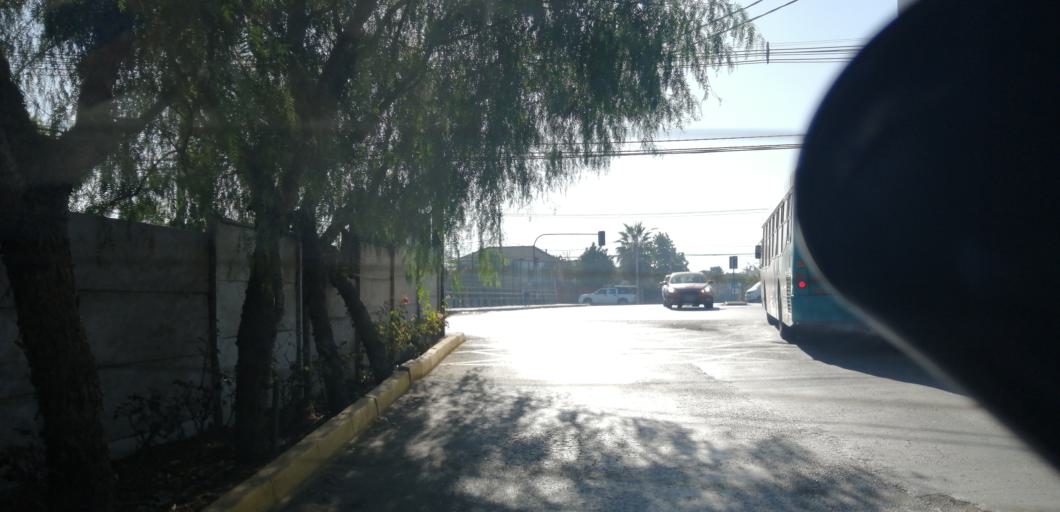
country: CL
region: Santiago Metropolitan
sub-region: Provincia de Santiago
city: Lo Prado
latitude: -33.4698
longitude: -70.7617
